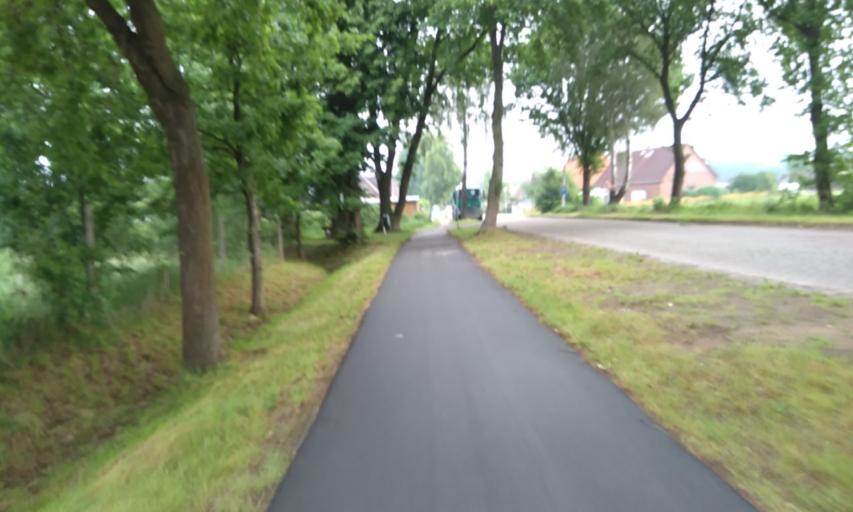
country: DE
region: Lower Saxony
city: Deinste
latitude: 53.5235
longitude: 9.4432
